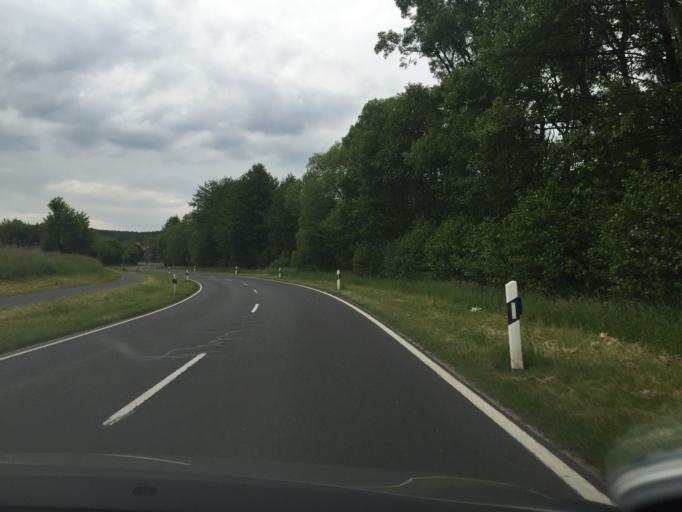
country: DE
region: Bavaria
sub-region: Regierungsbezirk Unterfranken
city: Hosbach
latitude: 50.0207
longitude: 9.2045
